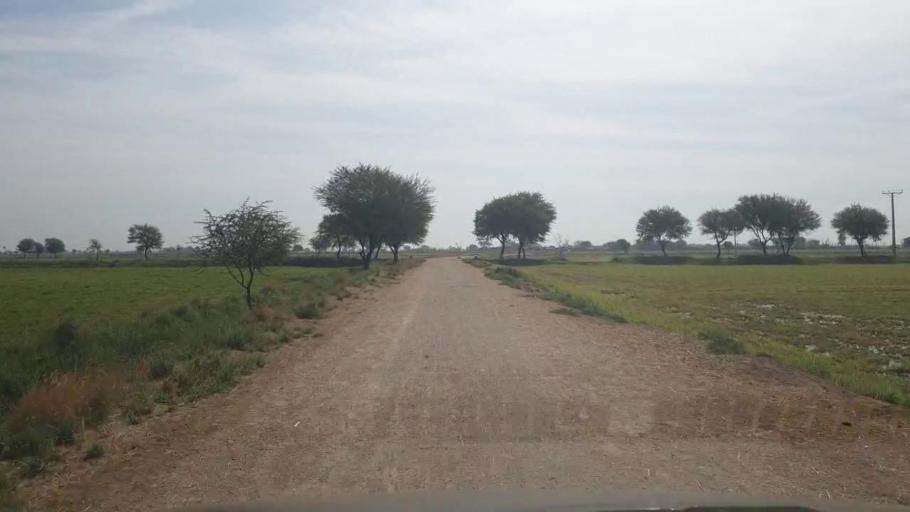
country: PK
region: Sindh
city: Umarkot
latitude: 25.3570
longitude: 69.6047
